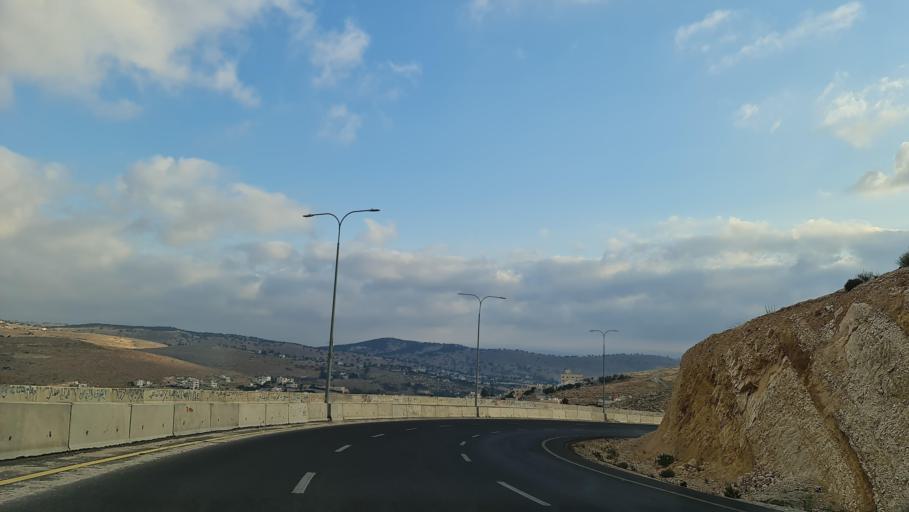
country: JO
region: Zarqa
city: Russeifa
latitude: 32.0912
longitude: 35.9605
